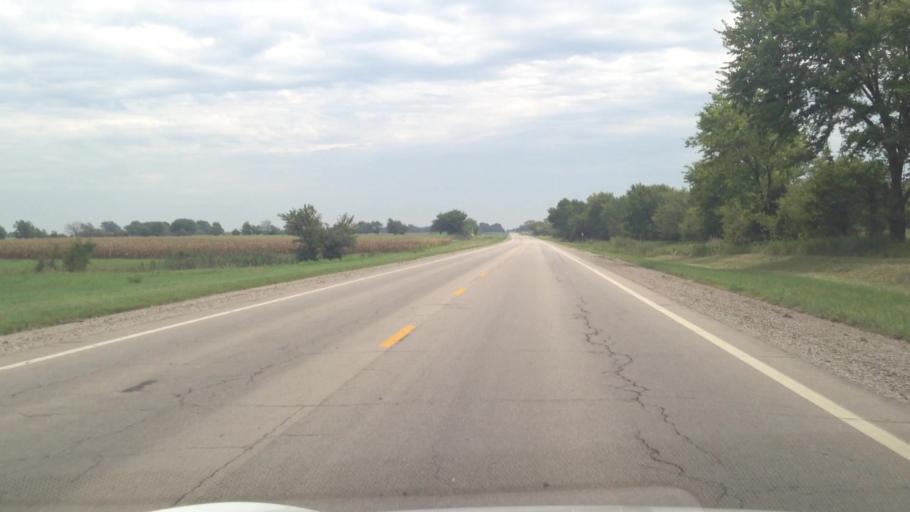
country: US
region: Kansas
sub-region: Crawford County
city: Girard
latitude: 37.5142
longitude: -94.8826
